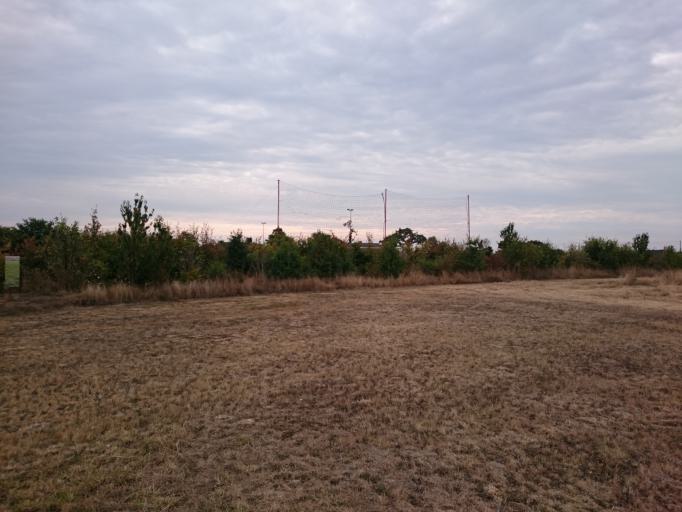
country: FR
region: Brittany
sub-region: Departement d'Ille-et-Vilaine
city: Pance
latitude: 47.8942
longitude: -1.6154
